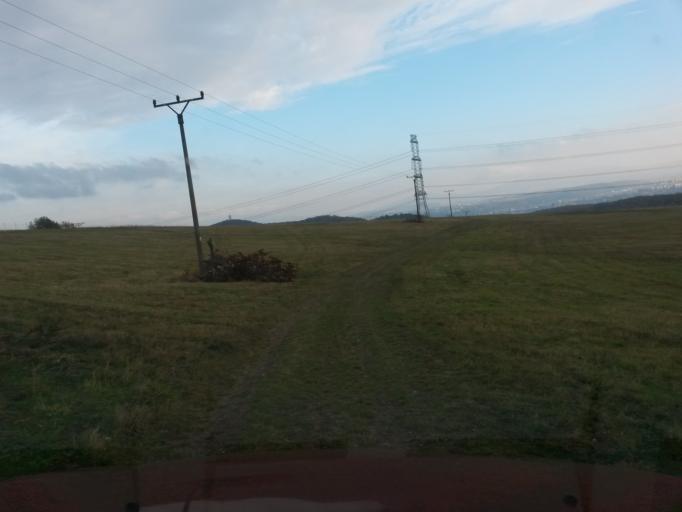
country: SK
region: Kosicky
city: Kosice
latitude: 48.7656
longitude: 21.2146
